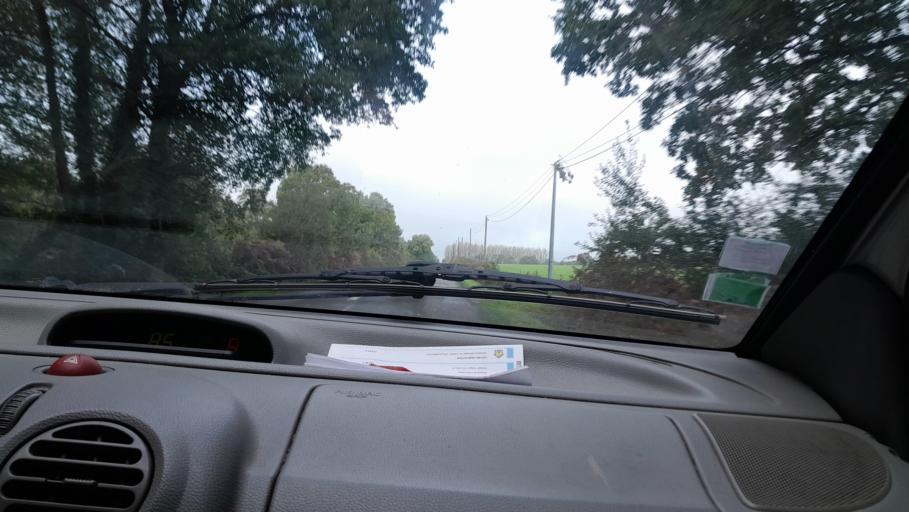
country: FR
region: Brittany
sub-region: Departement d'Ille-et-Vilaine
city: Luitre
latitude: 48.2272
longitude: -1.0995
